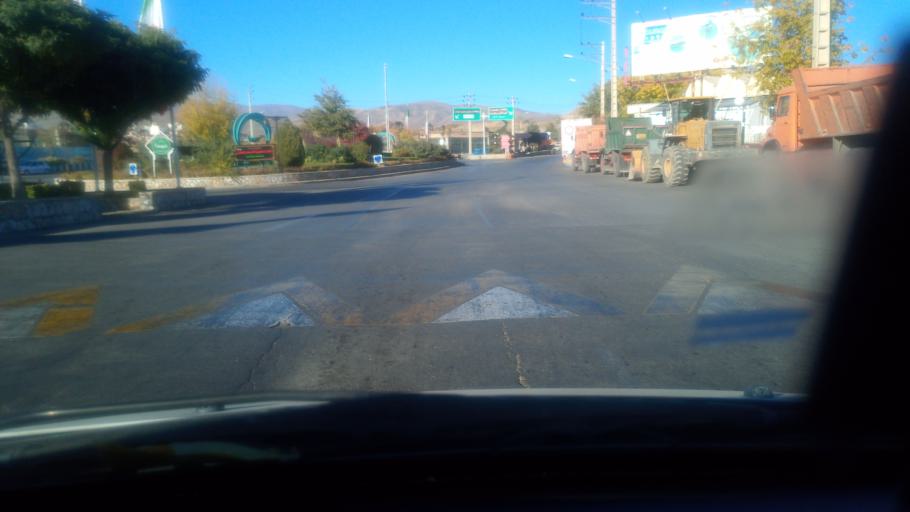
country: IR
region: Razavi Khorasan
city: Torqabeh
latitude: 36.3134
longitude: 59.3683
